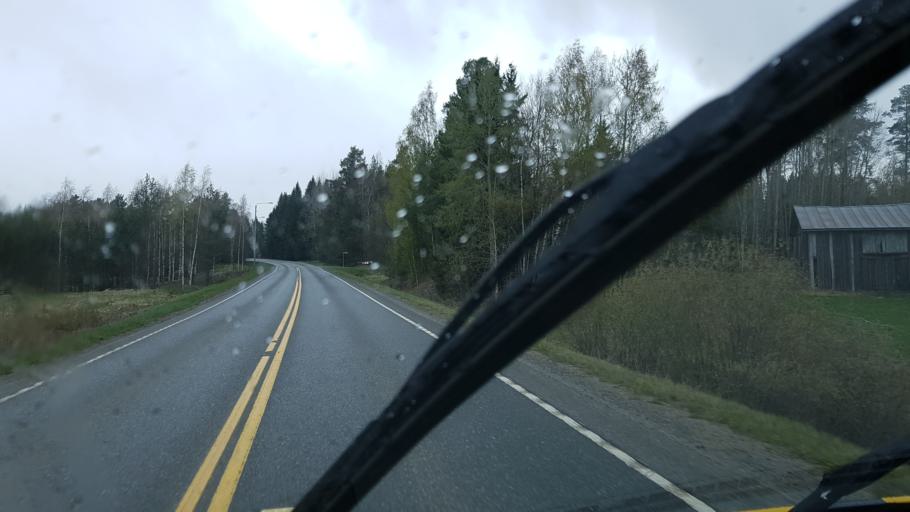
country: FI
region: Pirkanmaa
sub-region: Tampere
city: Pirkkala
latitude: 61.4265
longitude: 23.6332
